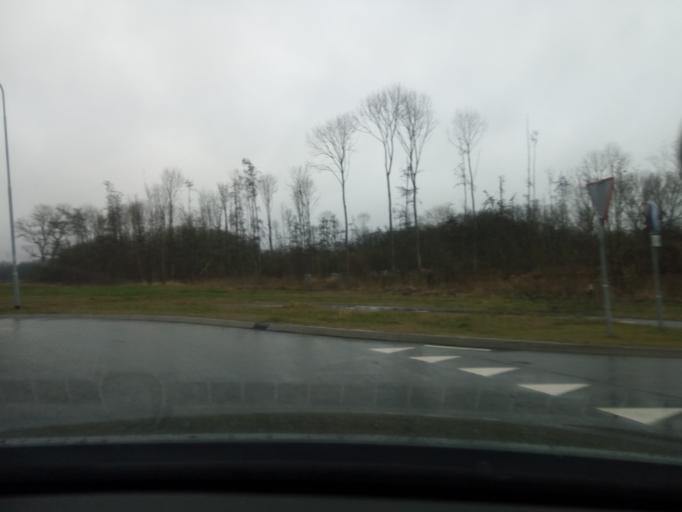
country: NL
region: Groningen
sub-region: Gemeente Appingedam
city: Appingedam
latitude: 53.3178
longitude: 6.7948
